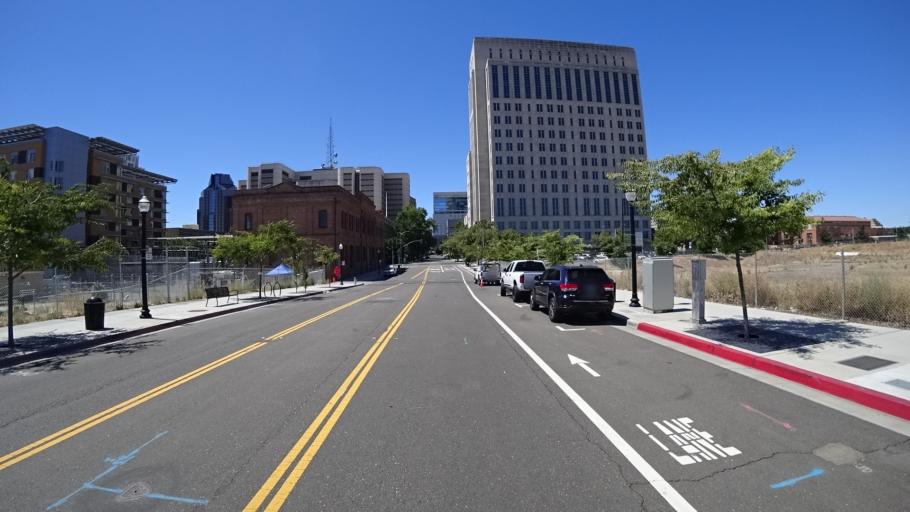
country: US
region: California
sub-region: Sacramento County
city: Sacramento
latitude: 38.5849
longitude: -121.4975
